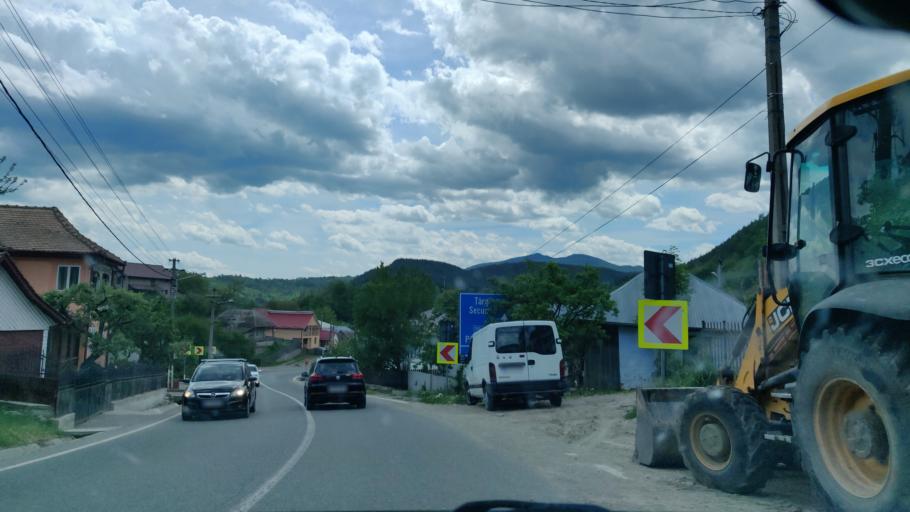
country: RO
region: Vrancea
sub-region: Comuna Tulnici
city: Tulnici
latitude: 45.9166
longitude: 26.6711
